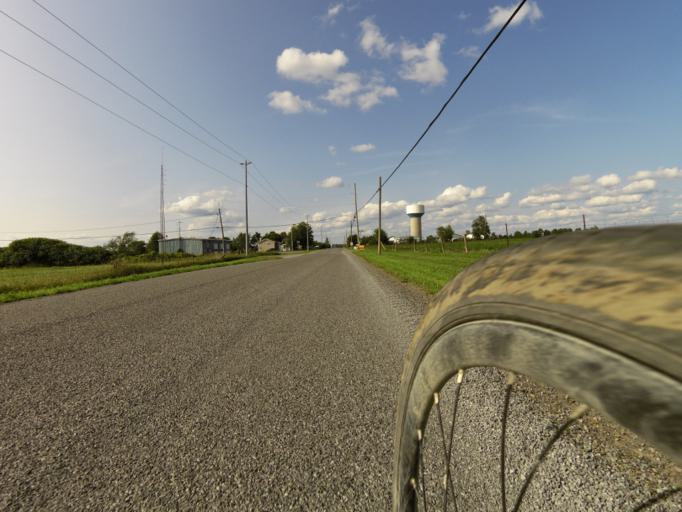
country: CA
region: Ontario
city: Kingston
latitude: 44.4009
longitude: -76.5963
